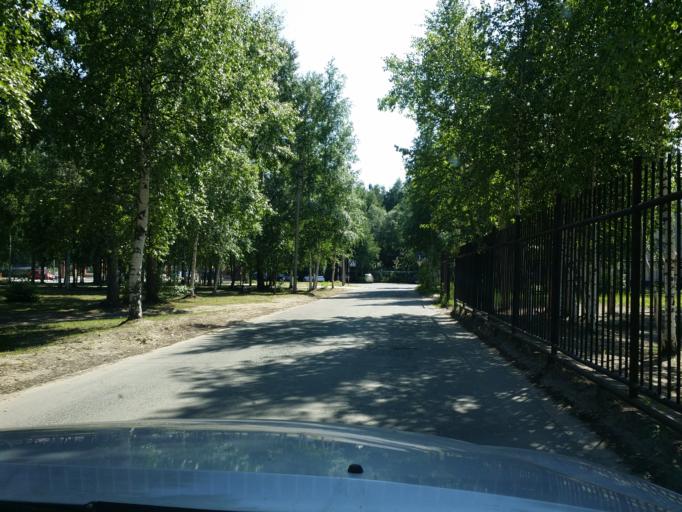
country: RU
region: Tomsk
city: Strezhevoy
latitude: 60.7260
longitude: 77.6024
